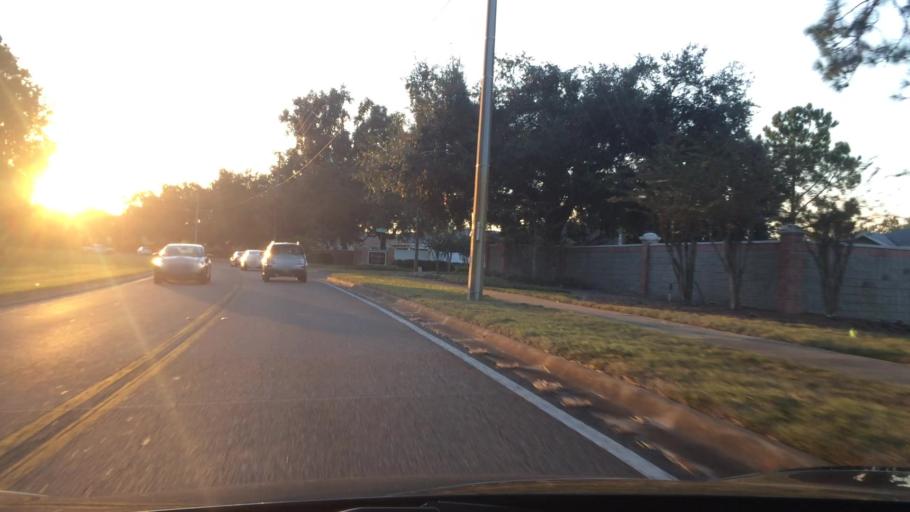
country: US
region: Florida
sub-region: Hillsborough County
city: Lutz
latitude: 28.1800
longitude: -82.4444
